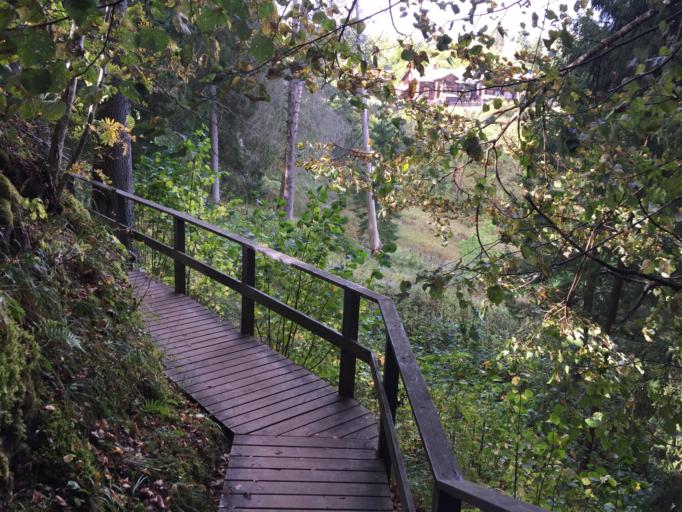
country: LV
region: Ligatne
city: Ligatne
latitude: 57.2305
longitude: 25.0433
